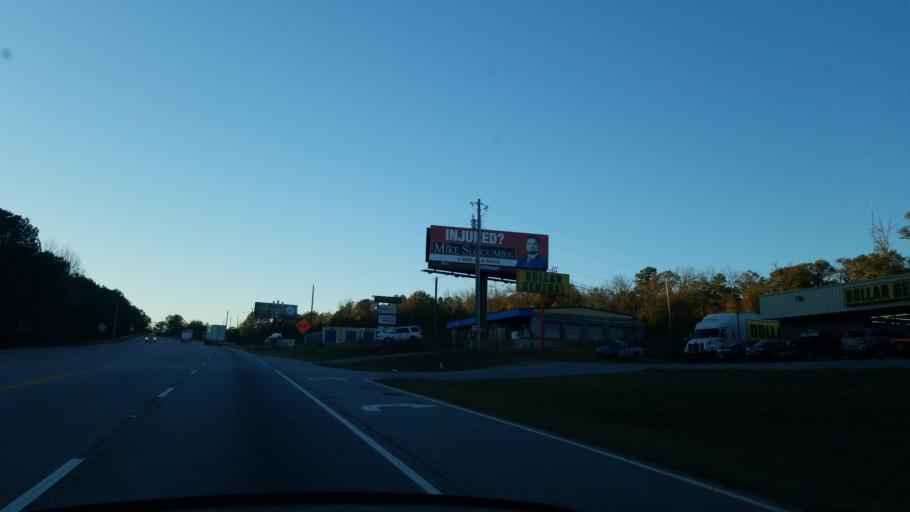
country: US
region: Georgia
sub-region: Chattahoochee County
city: Cusseta
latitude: 32.3019
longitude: -84.7840
